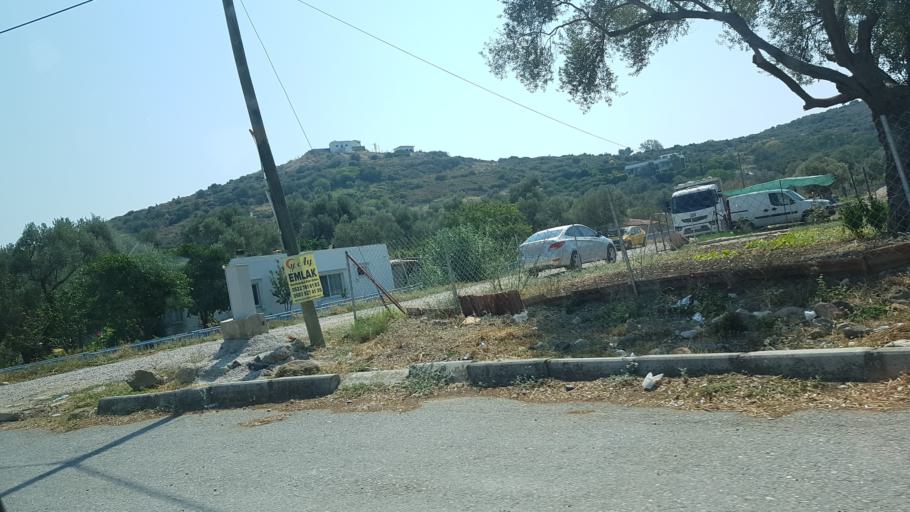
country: TR
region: Izmir
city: Urla
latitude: 38.3798
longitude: 26.7517
